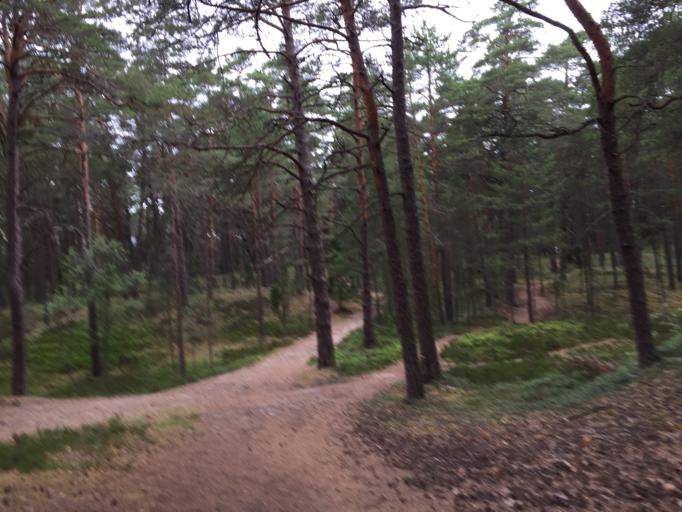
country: LV
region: Carnikava
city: Carnikava
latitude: 57.1230
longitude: 24.2158
